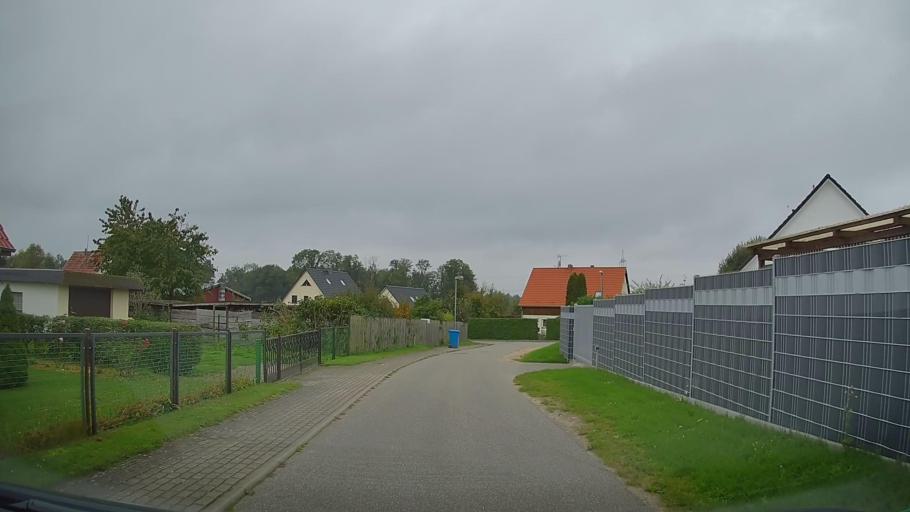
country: DE
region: Mecklenburg-Vorpommern
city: Guestrow
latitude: 53.8451
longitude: 12.1714
